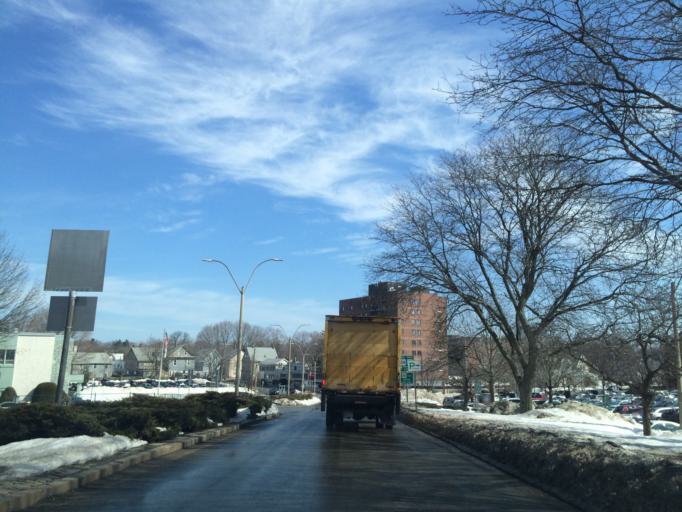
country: US
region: Massachusetts
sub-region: Middlesex County
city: Arlington
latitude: 42.4159
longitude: -71.1524
